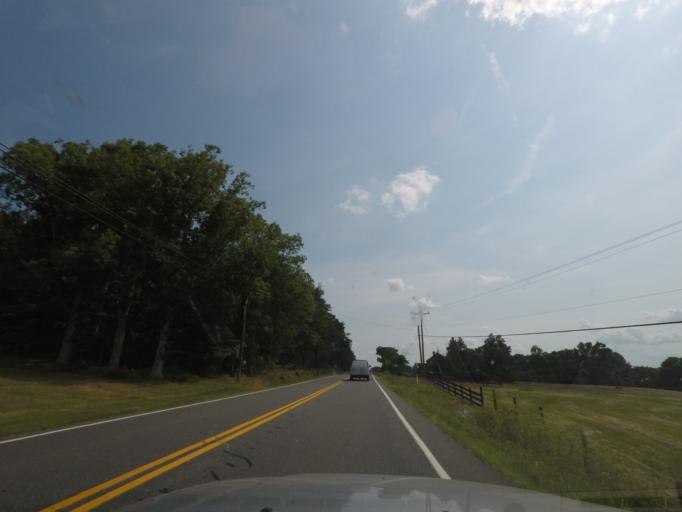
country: US
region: Virginia
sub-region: Fluvanna County
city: Palmyra
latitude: 37.8704
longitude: -78.2609
